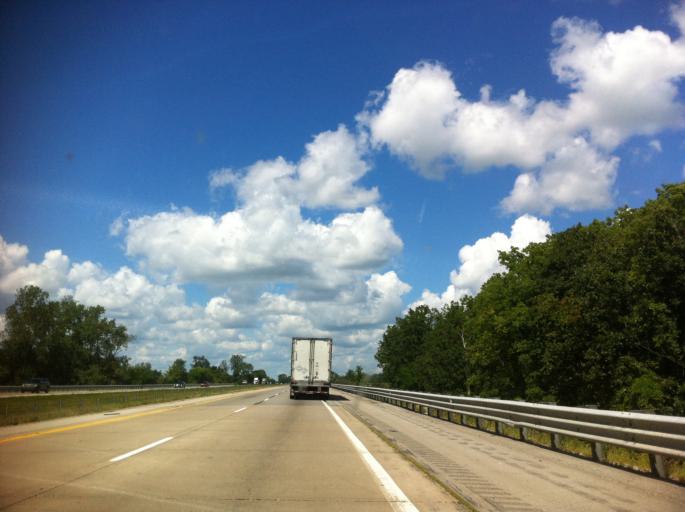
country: US
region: Michigan
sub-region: Monroe County
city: Dundee
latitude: 41.9843
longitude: -83.6785
